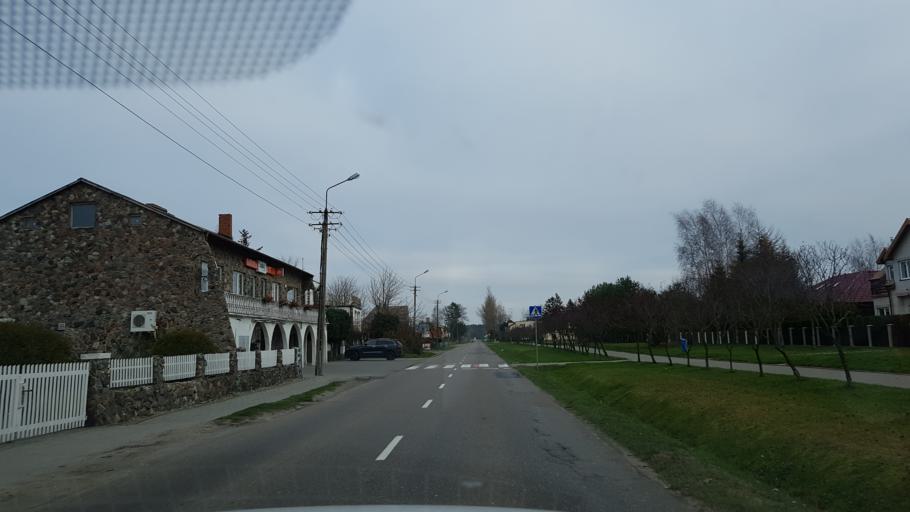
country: PL
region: West Pomeranian Voivodeship
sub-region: Powiat kolobrzeski
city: Grzybowo
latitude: 54.1589
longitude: 15.4880
